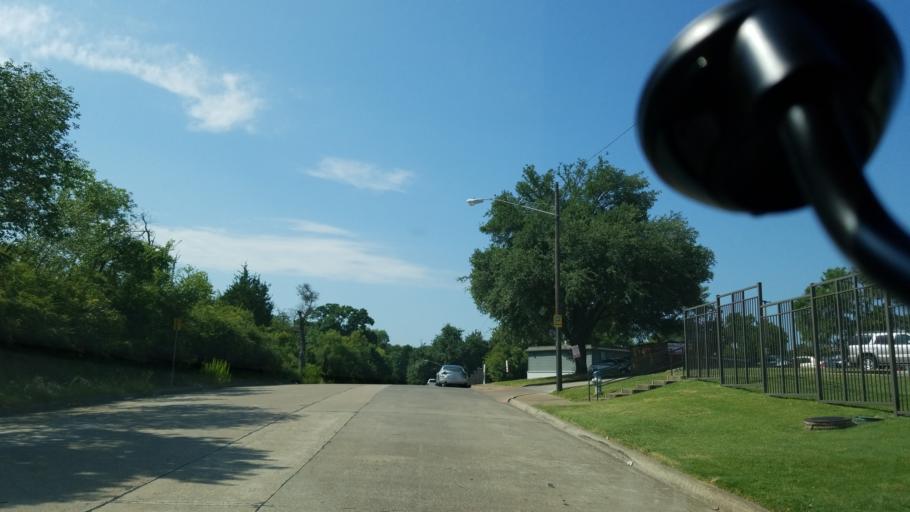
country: US
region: Texas
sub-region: Dallas County
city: Cockrell Hill
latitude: 32.7075
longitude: -96.8659
